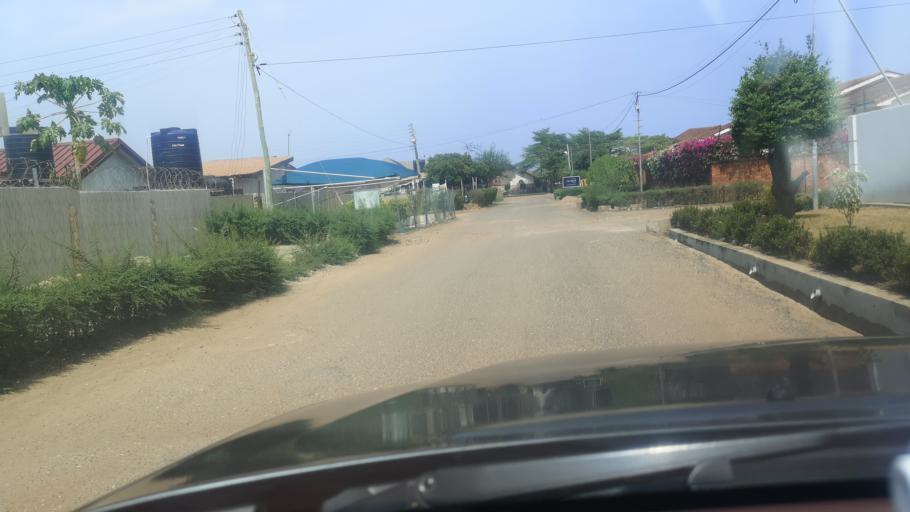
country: GH
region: Greater Accra
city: Nungua
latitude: 5.6503
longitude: -0.0751
